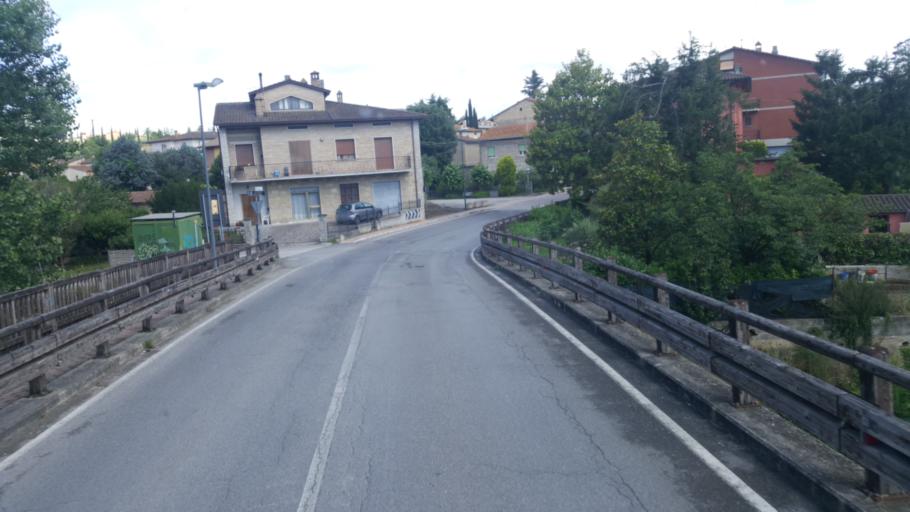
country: IT
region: Umbria
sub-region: Provincia di Perugia
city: Torgiano
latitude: 43.0248
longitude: 12.4461
